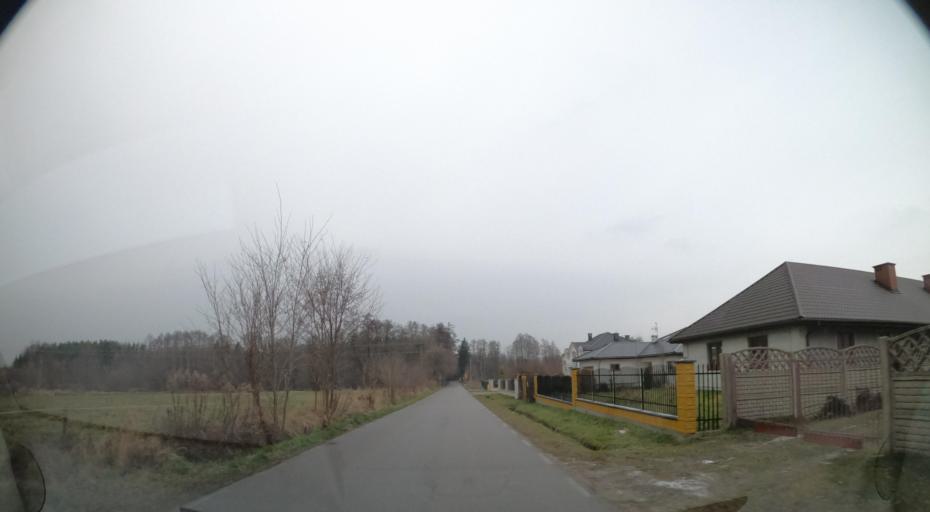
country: PL
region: Masovian Voivodeship
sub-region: Powiat radomski
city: Jastrzebia
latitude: 51.4221
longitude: 21.2265
